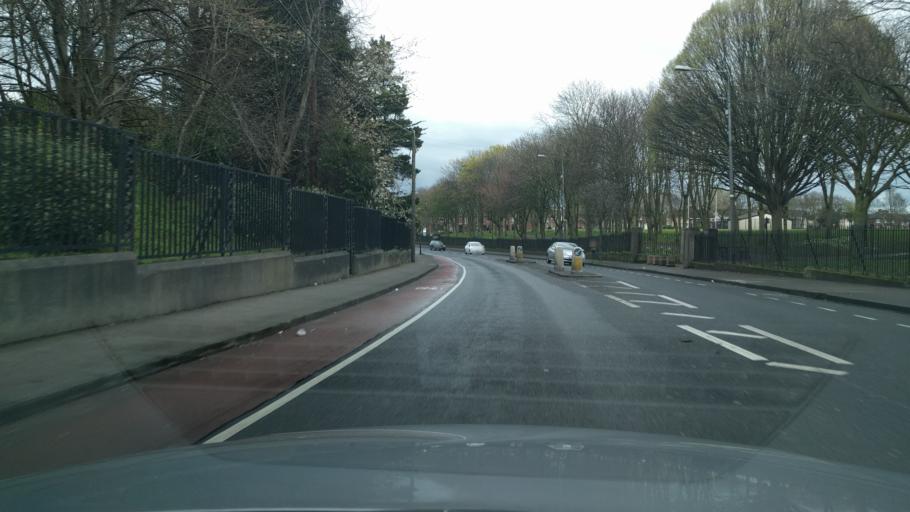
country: IE
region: Leinster
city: Chapelizod
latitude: 53.3419
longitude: -6.3415
